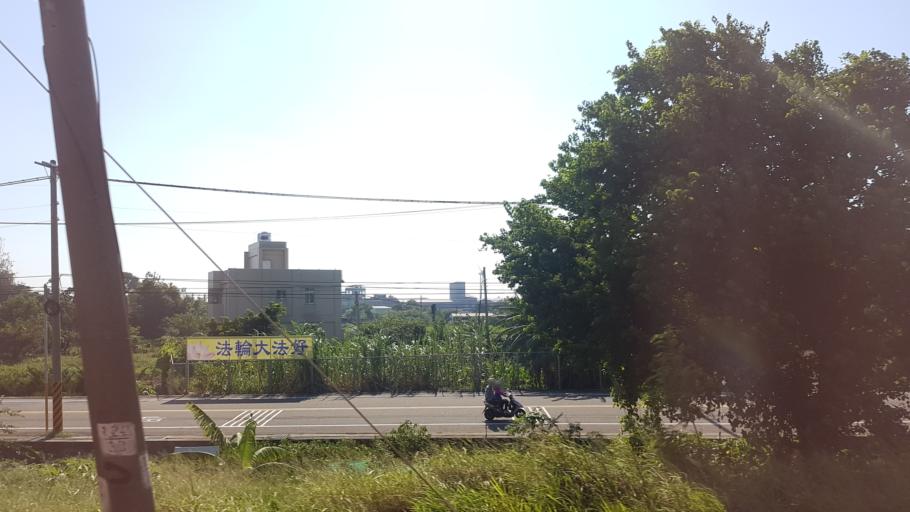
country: TW
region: Taiwan
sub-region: Hsinchu
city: Hsinchu
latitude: 24.7083
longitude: 120.8704
